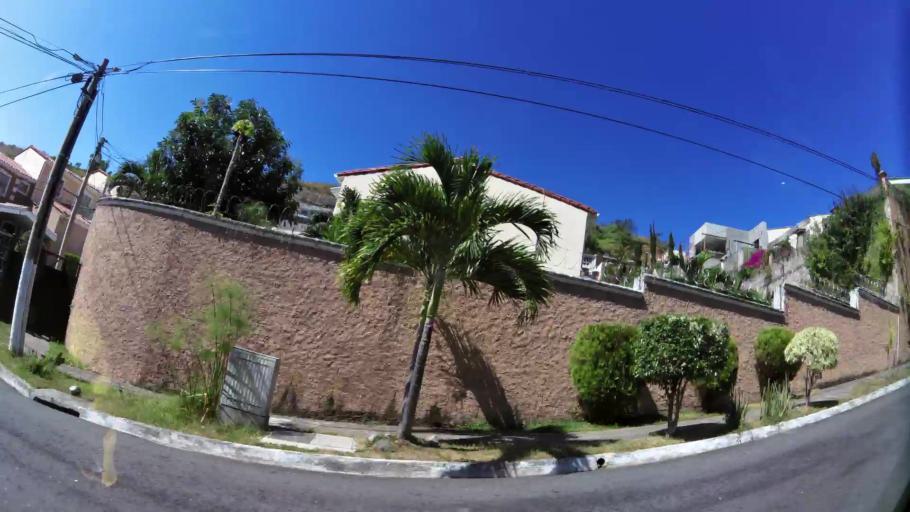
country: SV
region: La Libertad
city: Nuevo Cuscatlan
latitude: 13.6418
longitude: -89.2801
